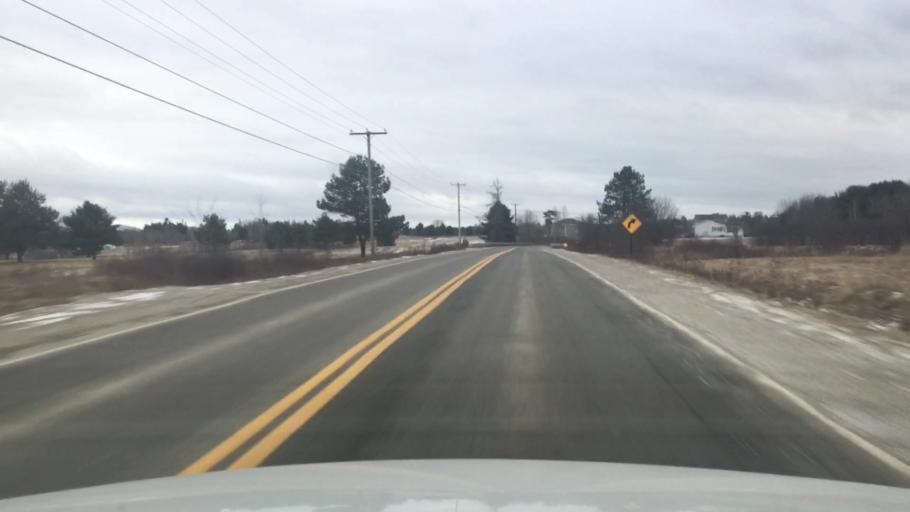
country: US
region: Maine
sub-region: Hancock County
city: Trenton
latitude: 44.4931
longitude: -68.3631
